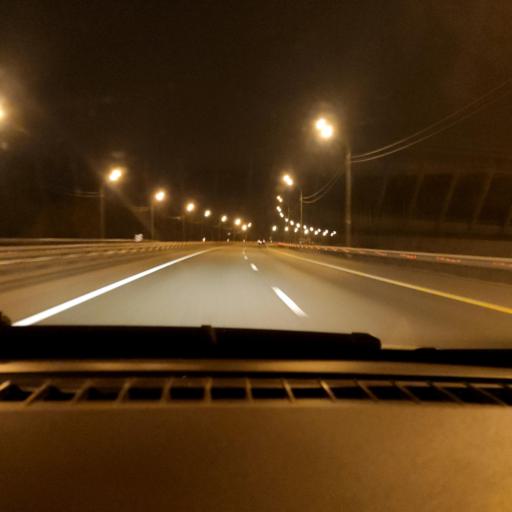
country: RU
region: Lipetsk
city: Khlevnoye
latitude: 52.2561
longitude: 39.0661
